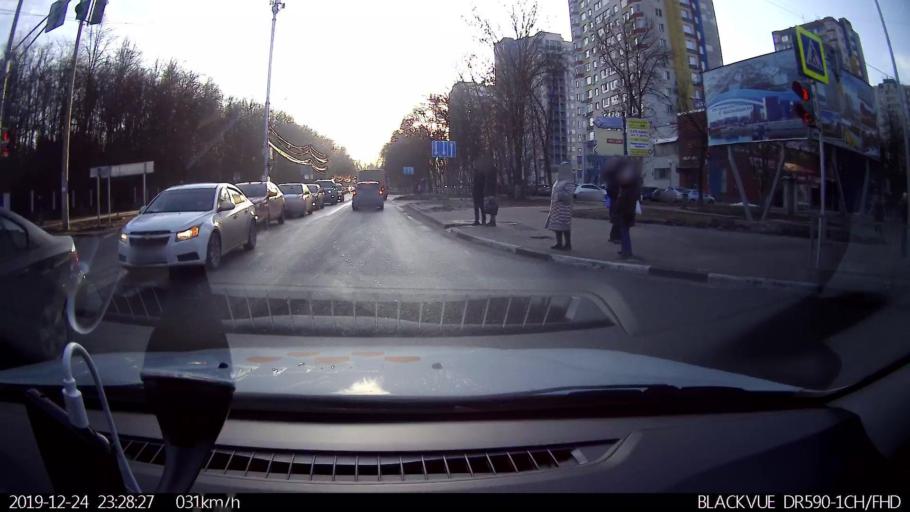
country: RU
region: Nizjnij Novgorod
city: Gorbatovka
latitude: 56.2429
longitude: 43.8493
